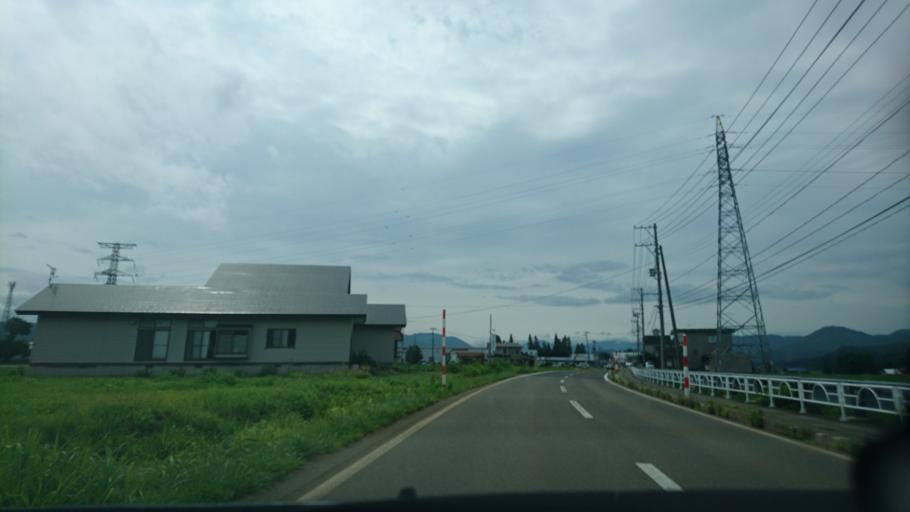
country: JP
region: Akita
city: Yuzawa
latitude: 39.1821
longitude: 140.5542
